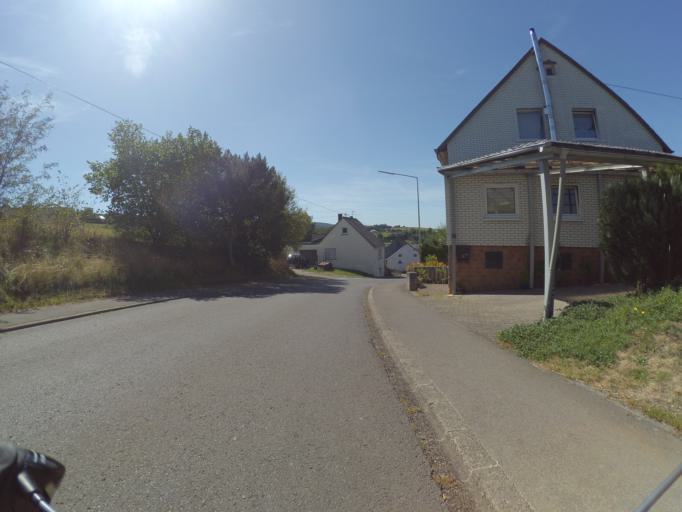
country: DE
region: Rheinland-Pfalz
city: Rorodt
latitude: 49.7736
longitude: 7.0892
